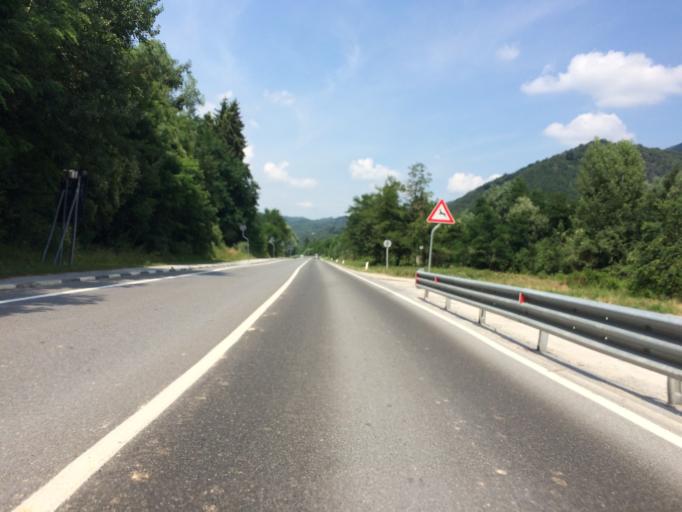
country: IT
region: Piedmont
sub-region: Provincia di Cuneo
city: Vernante
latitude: 44.2646
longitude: 7.5180
